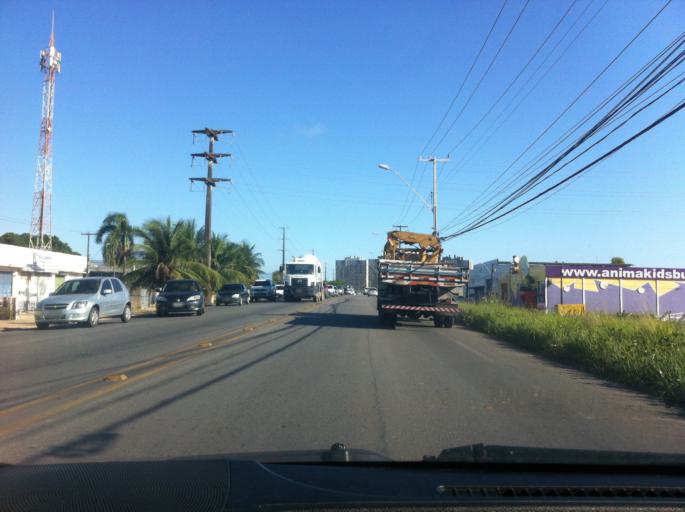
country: BR
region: Alagoas
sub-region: Maceio
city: Maceio
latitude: -9.5848
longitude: -35.7340
